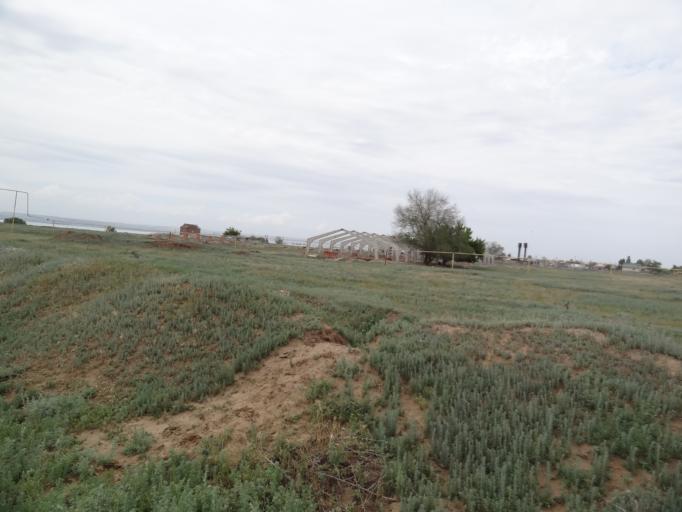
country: RU
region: Saratov
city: Privolzhskiy
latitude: 51.1953
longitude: 45.9139
